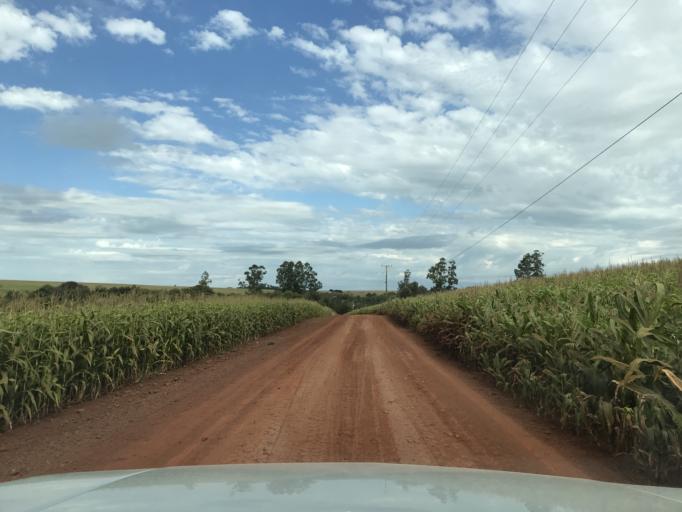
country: BR
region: Parana
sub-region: Palotina
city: Palotina
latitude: -24.3192
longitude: -53.8066
